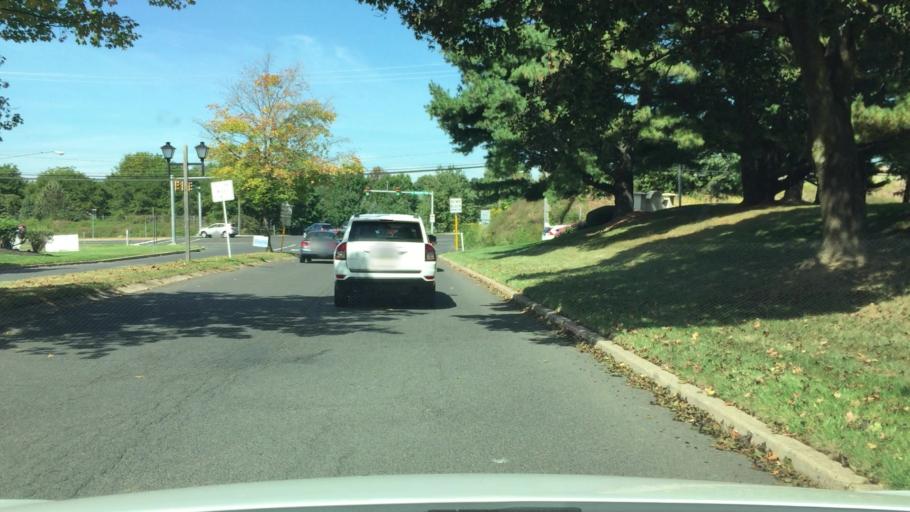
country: US
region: Pennsylvania
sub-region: Bucks County
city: Newtown
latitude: 40.2178
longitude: -74.9257
